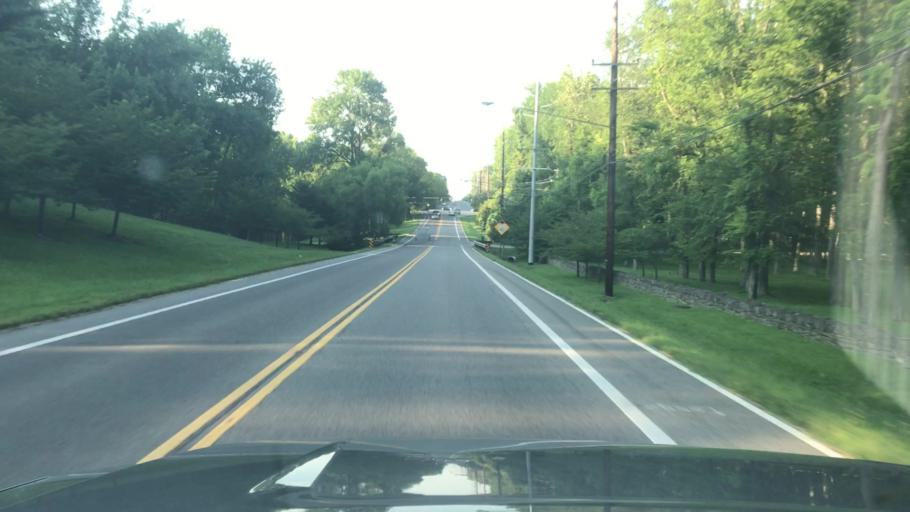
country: US
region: Tennessee
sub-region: Davidson County
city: Forest Hills
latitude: 36.0867
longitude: -86.8302
